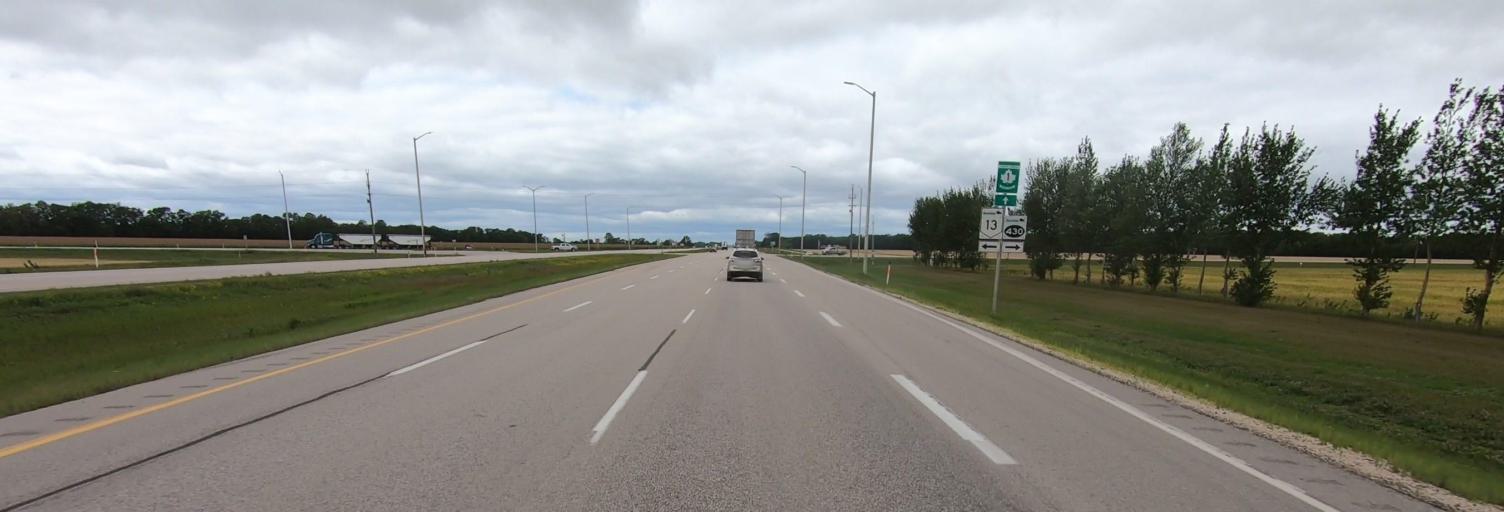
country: CA
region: Manitoba
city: Portage la Prairie
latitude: 49.9536
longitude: -98.0087
